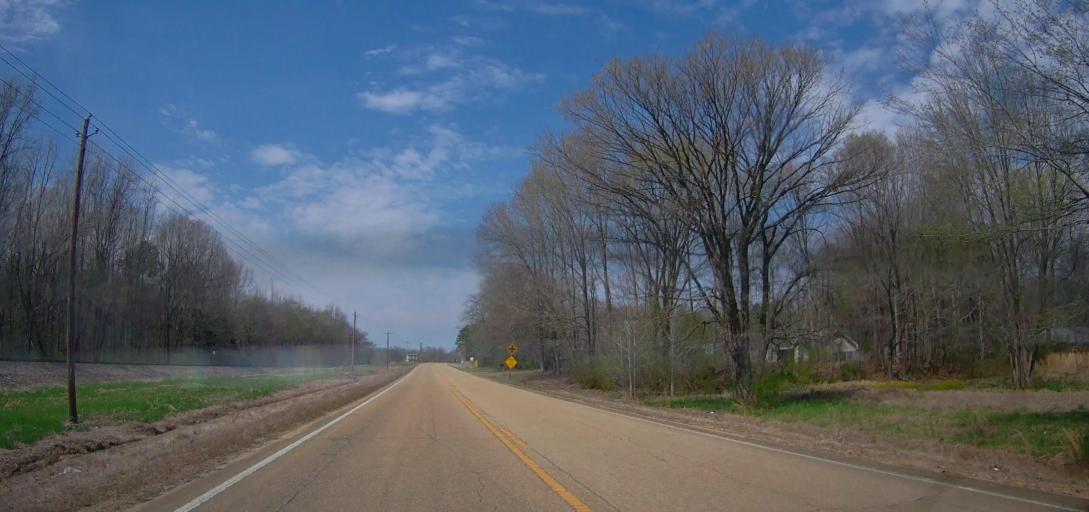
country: US
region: Mississippi
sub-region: Benton County
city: Ashland
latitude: 34.6294
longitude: -89.2681
